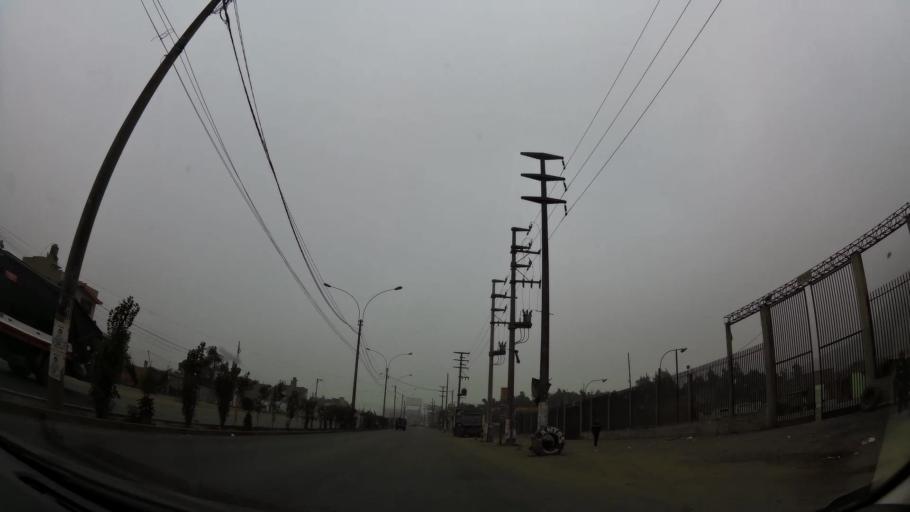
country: PE
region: Lima
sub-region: Lima
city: Santa Maria
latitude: -12.0064
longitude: -76.8498
